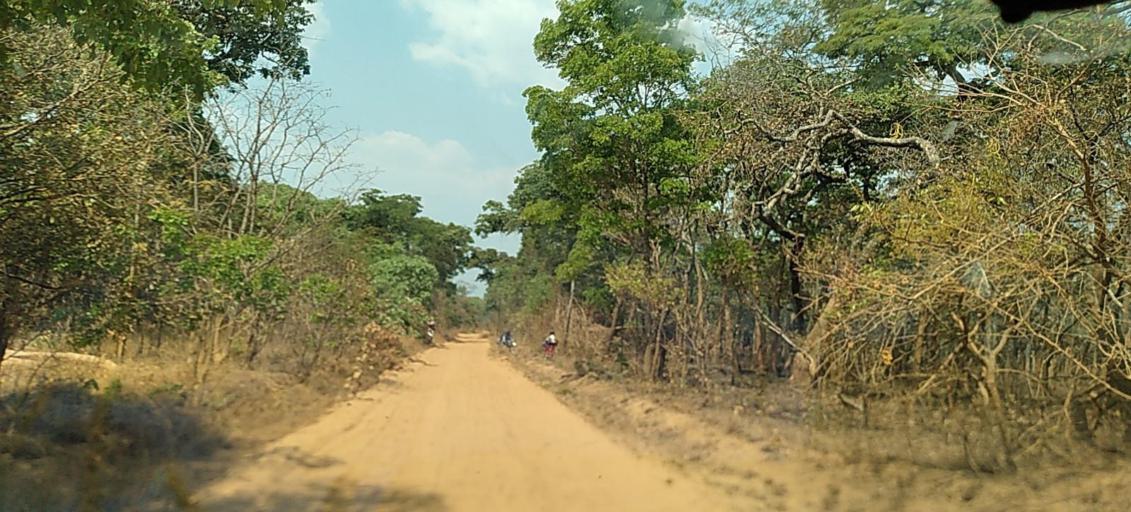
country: ZM
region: North-Western
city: Kasempa
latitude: -13.3208
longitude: 26.0431
